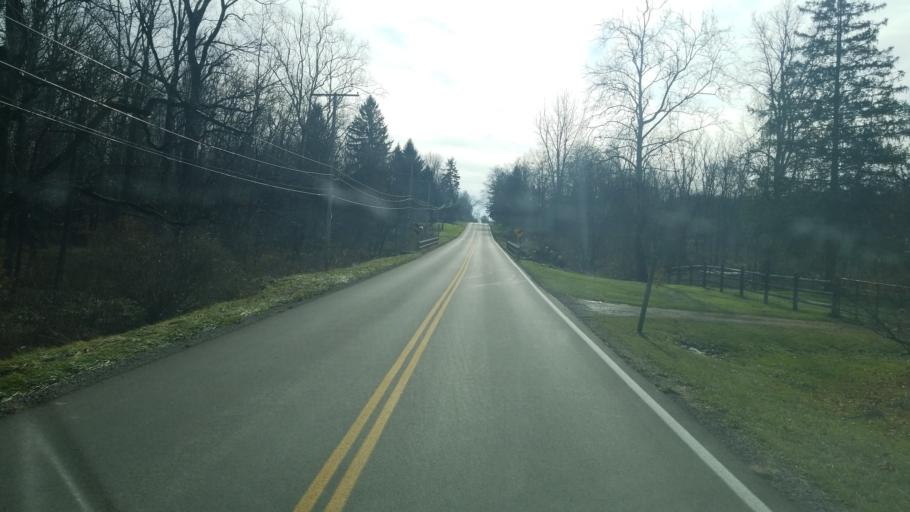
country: US
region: Ohio
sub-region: Ashtabula County
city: Roaming Shores
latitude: 41.6647
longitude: -80.9145
